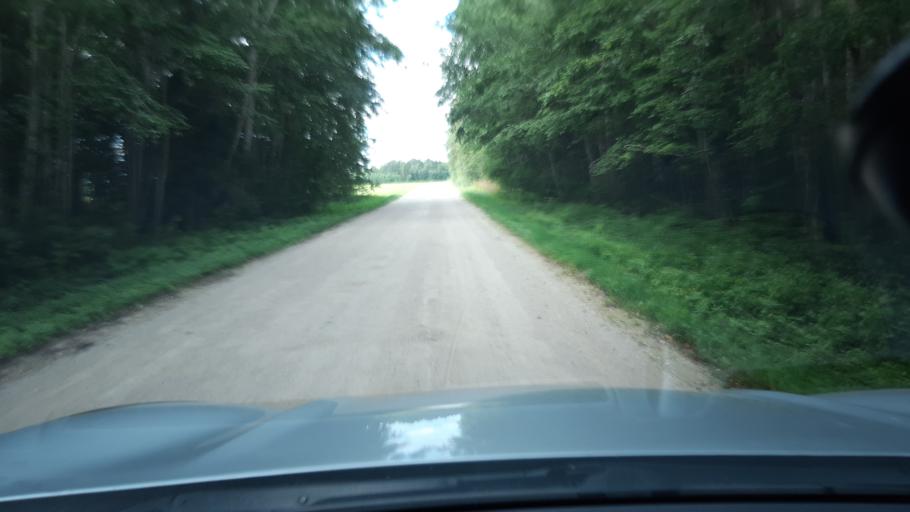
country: EE
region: Paernumaa
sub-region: Vaendra vald (alev)
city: Vandra
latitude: 58.7846
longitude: 25.0358
